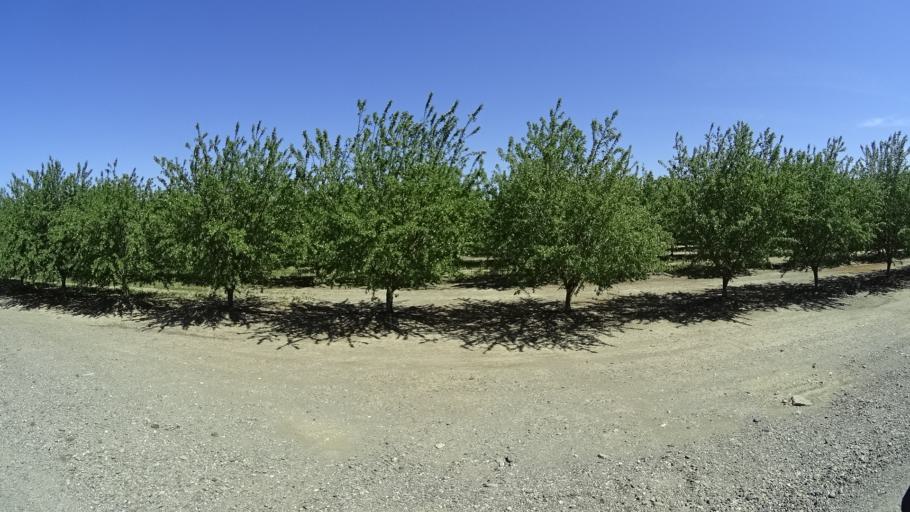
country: US
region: California
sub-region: Glenn County
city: Orland
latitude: 39.7575
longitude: -122.1598
